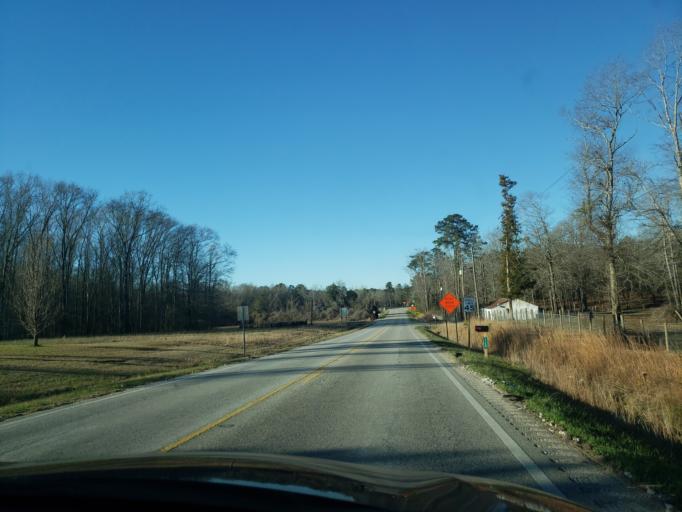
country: US
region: Alabama
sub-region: Macon County
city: Tuskegee
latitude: 32.5735
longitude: -85.6587
